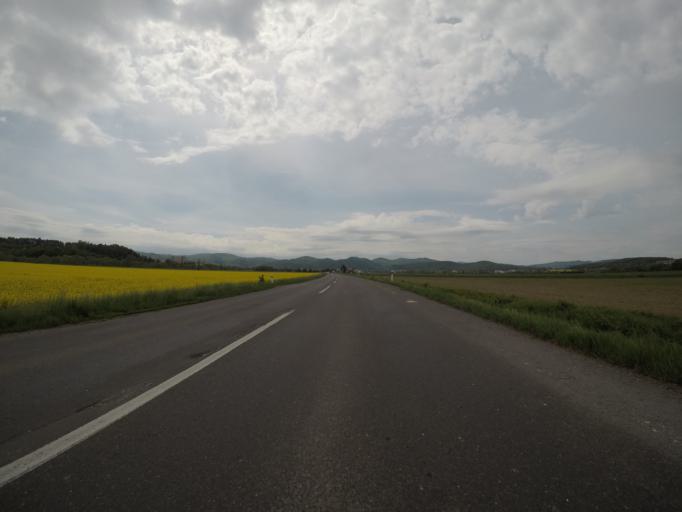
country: SK
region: Banskobystricky
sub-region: Okres Banska Bystrica
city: Zvolen
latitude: 48.6044
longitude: 19.1257
